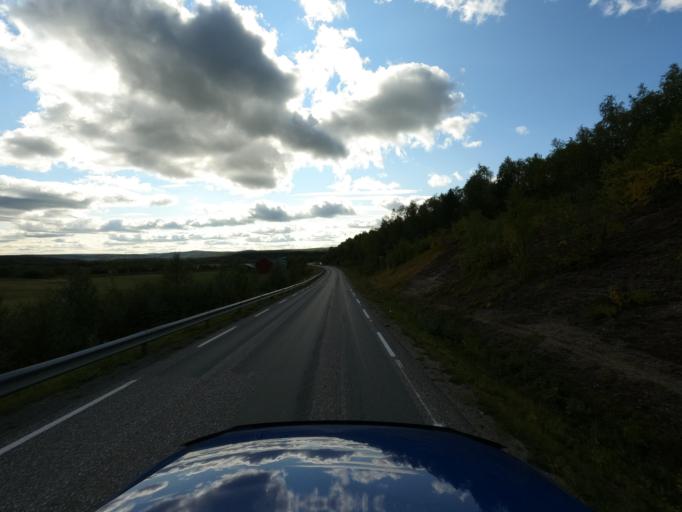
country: NO
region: Finnmark Fylke
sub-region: Karasjok
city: Karasjohka
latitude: 69.4262
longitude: 25.7939
